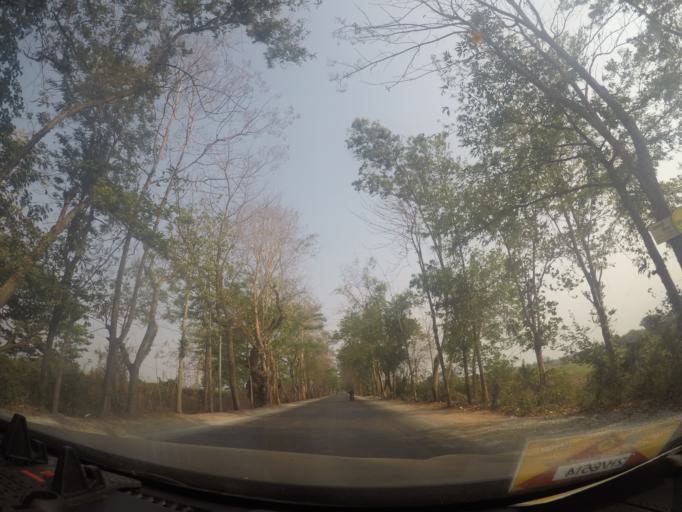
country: MM
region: Bago
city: Paungde
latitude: 18.4487
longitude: 95.5400
